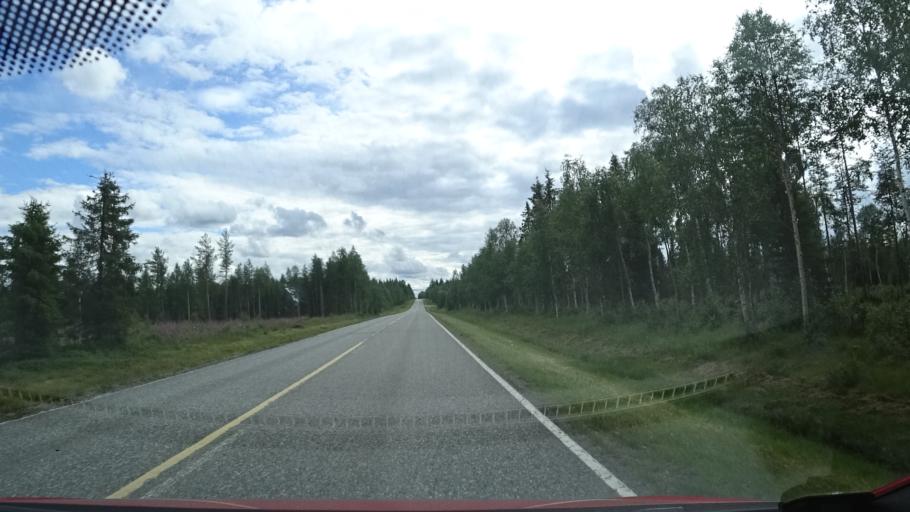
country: FI
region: Lapland
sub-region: Tunturi-Lappi
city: Kittilae
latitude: 67.4773
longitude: 24.9332
